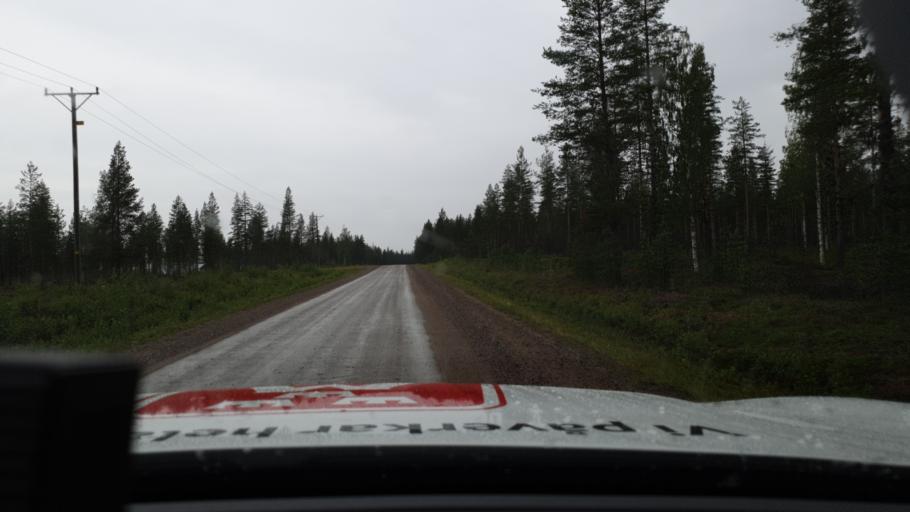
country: SE
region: Norrbotten
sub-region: Bodens Kommun
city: Boden
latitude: 66.3011
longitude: 21.3289
